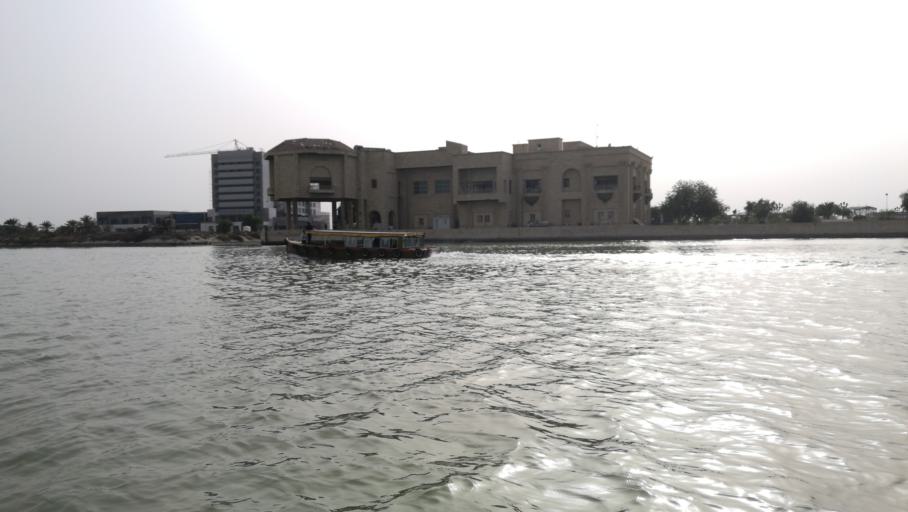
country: IQ
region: Basra Governorate
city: Al Basrah al Qadimah
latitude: 30.4969
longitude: 47.8650
